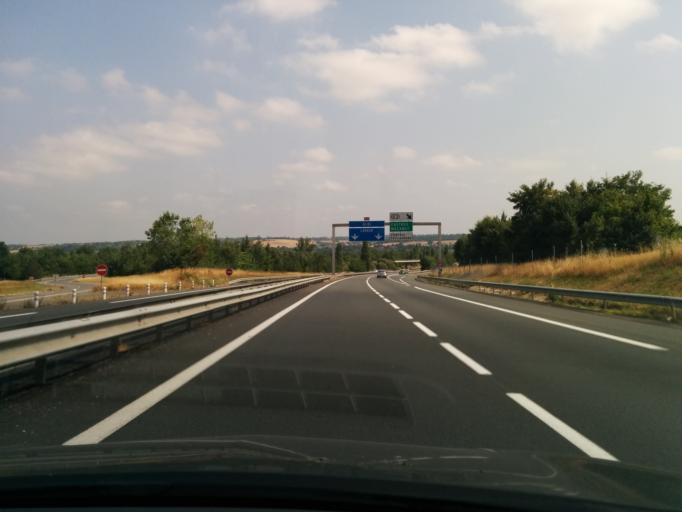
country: FR
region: Midi-Pyrenees
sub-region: Departement de la Haute-Garonne
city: Gragnague
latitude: 43.6827
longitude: 1.5618
